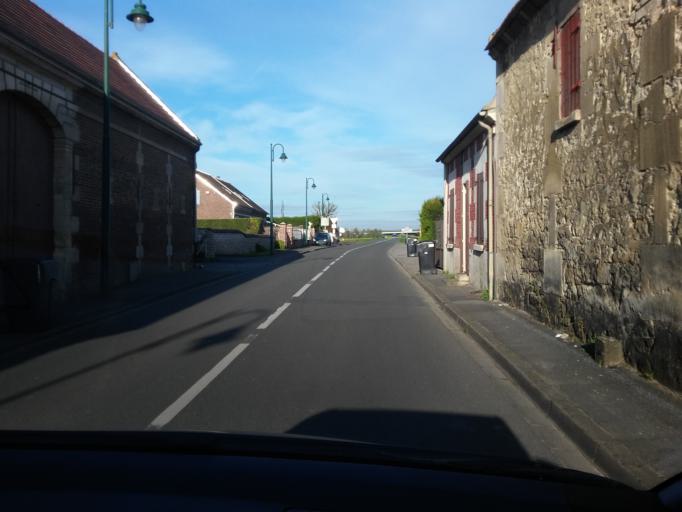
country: FR
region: Picardie
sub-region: Departement de l'Oise
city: Longueil-Sainte-Marie
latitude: 49.3499
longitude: 2.7167
